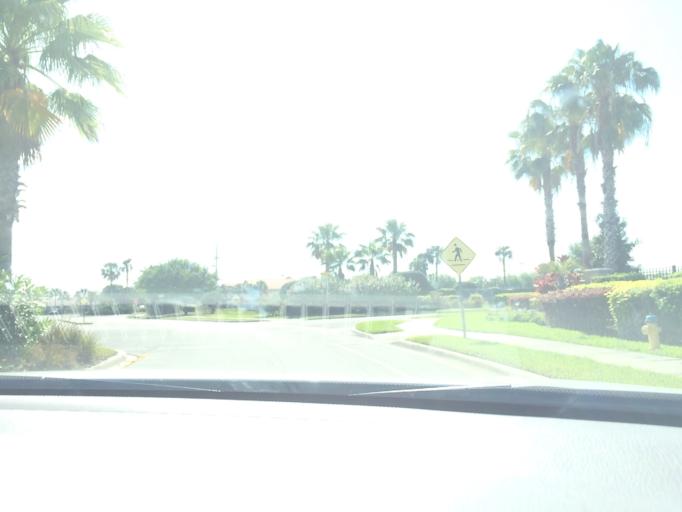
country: US
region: Florida
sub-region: Sarasota County
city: North Sarasota
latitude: 27.3921
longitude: -82.5152
